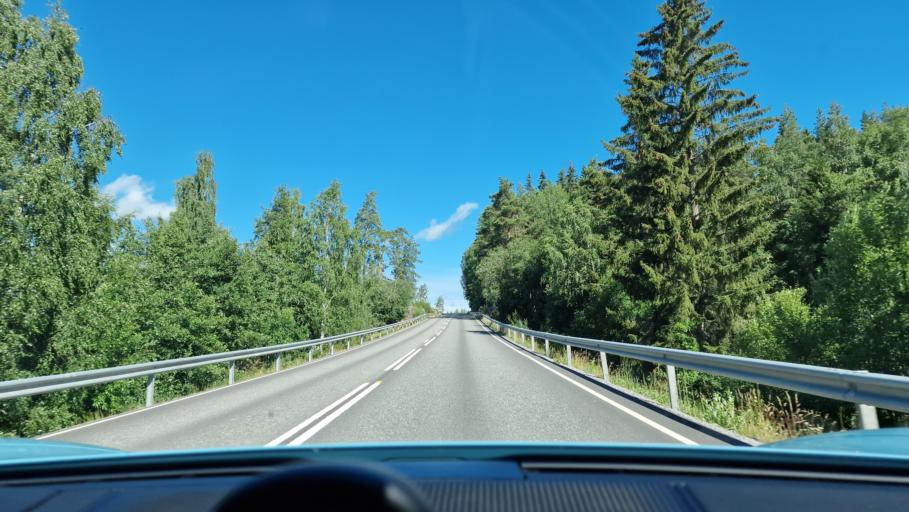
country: FI
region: Pirkanmaa
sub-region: Tampere
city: Sahalahti
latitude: 61.5706
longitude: 24.3017
